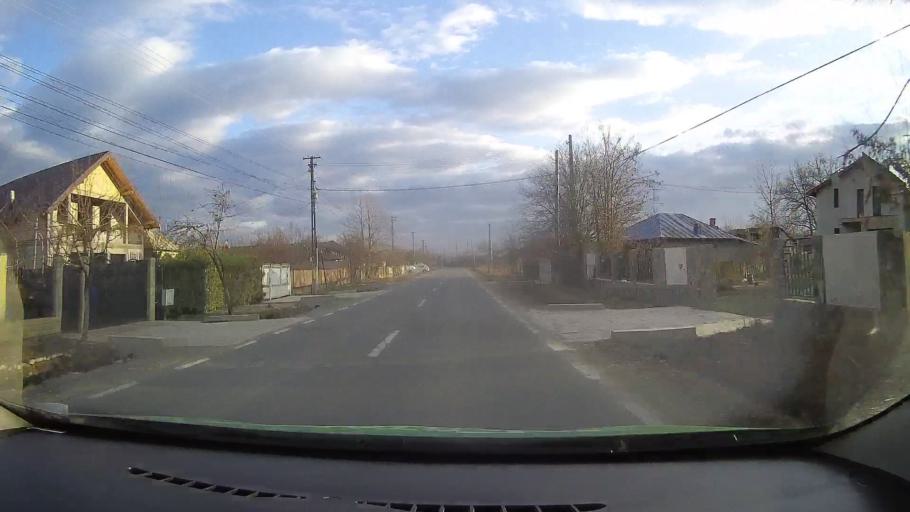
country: RO
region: Dambovita
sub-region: Comuna I. L. Caragiale
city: Ghirdoveni
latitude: 44.9539
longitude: 25.6578
